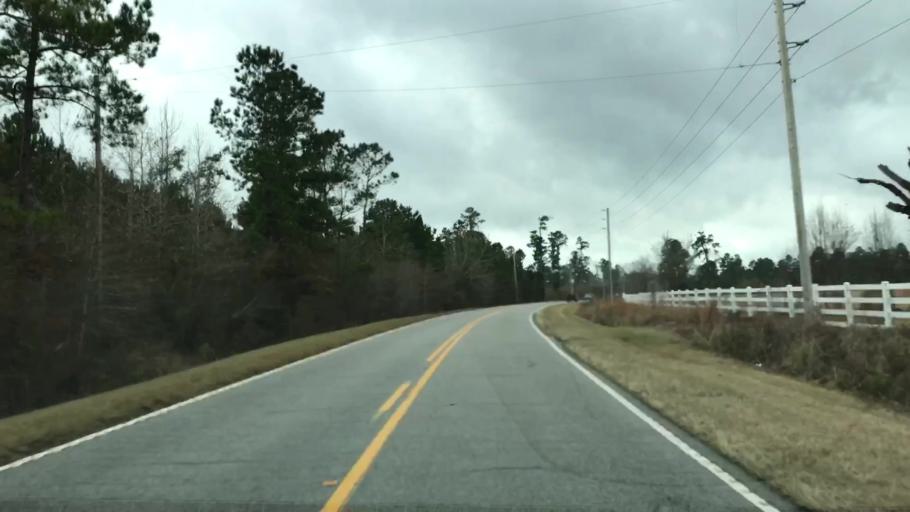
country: US
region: South Carolina
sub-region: Florence County
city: Johnsonville
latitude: 33.6501
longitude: -79.4195
